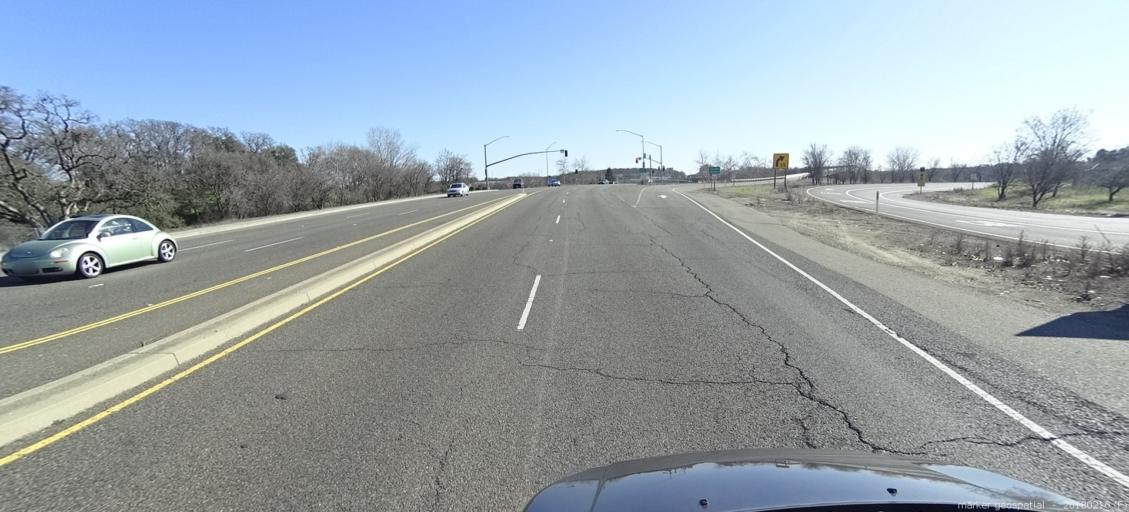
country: US
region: California
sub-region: Sacramento County
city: Folsom
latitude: 38.6442
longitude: -121.1576
